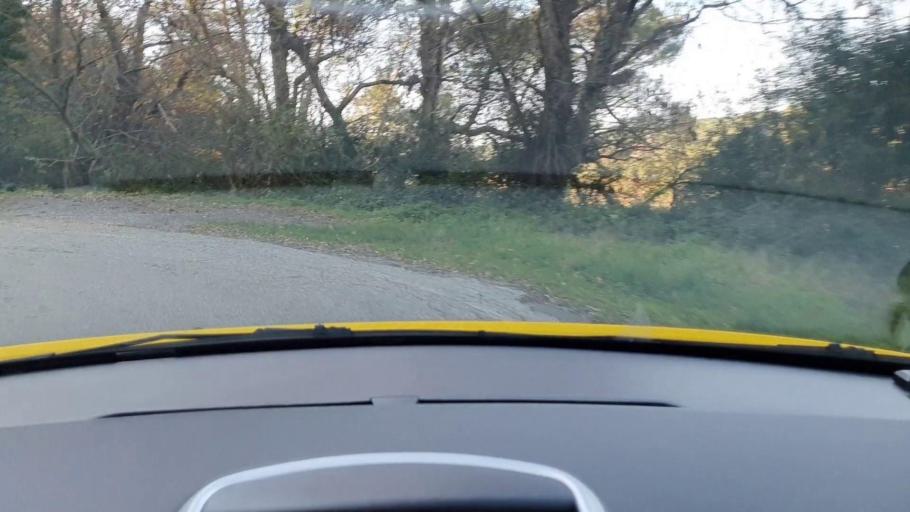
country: FR
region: Languedoc-Roussillon
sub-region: Departement du Gard
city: Branoux-les-Taillades
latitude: 44.2523
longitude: 3.9752
